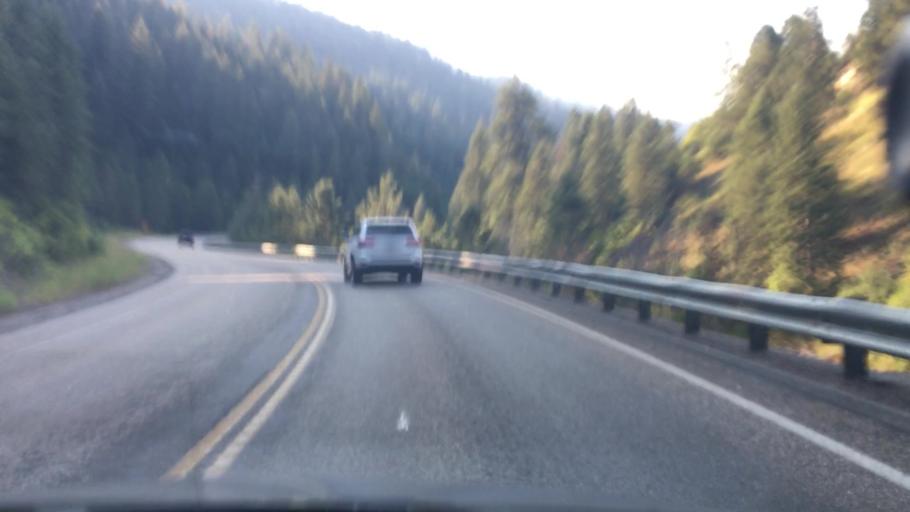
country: US
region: Idaho
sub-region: Valley County
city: Cascade
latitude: 44.1503
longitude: -116.1126
